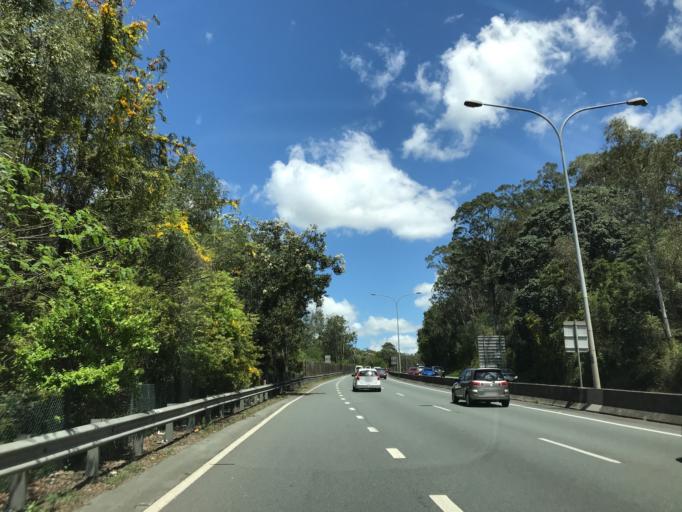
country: AU
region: Queensland
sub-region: Brisbane
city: Kenmore Hills
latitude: -27.5186
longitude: 152.9536
